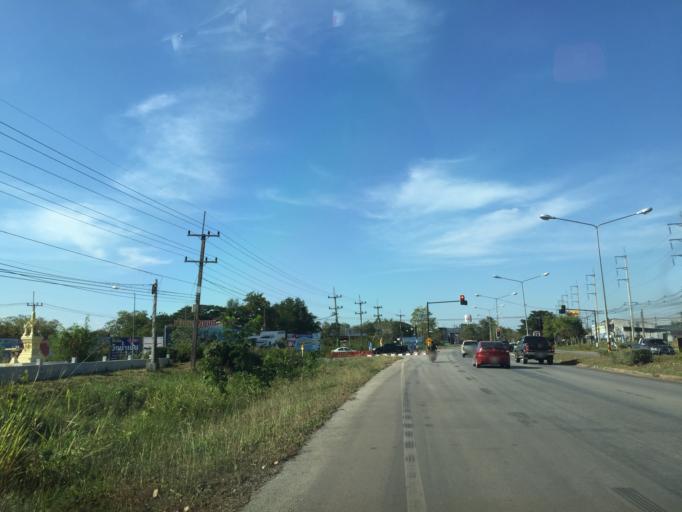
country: TH
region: Loei
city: Wang Saphung
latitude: 17.3233
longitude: 101.7610
